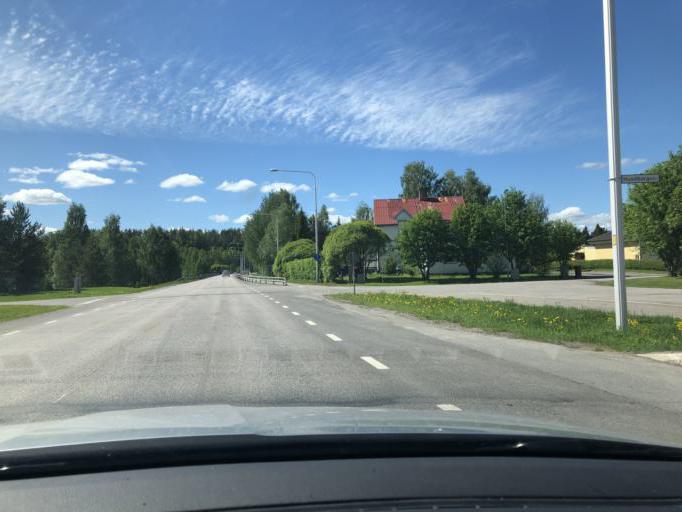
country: SE
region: Norrbotten
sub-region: Alvsbyns Kommun
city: AElvsbyn
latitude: 65.6675
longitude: 21.0405
